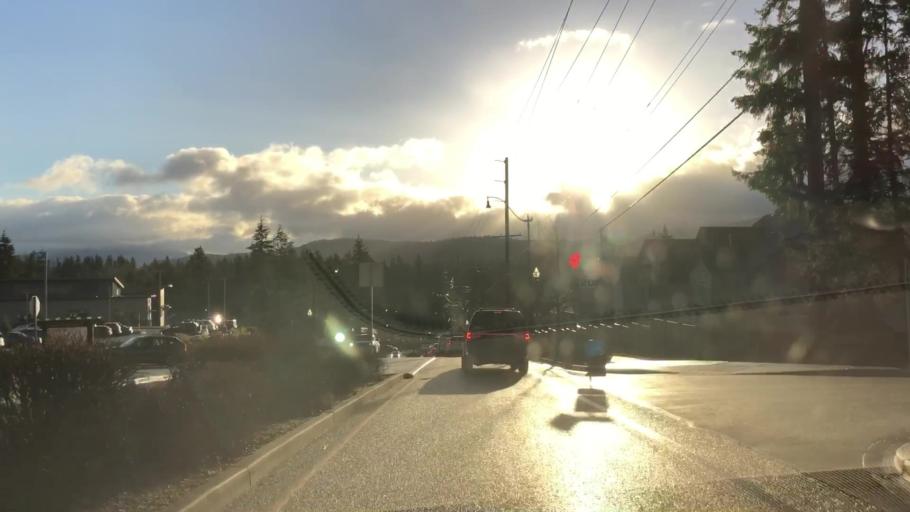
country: US
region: Washington
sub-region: King County
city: City of Sammamish
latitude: 47.5801
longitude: -122.0304
